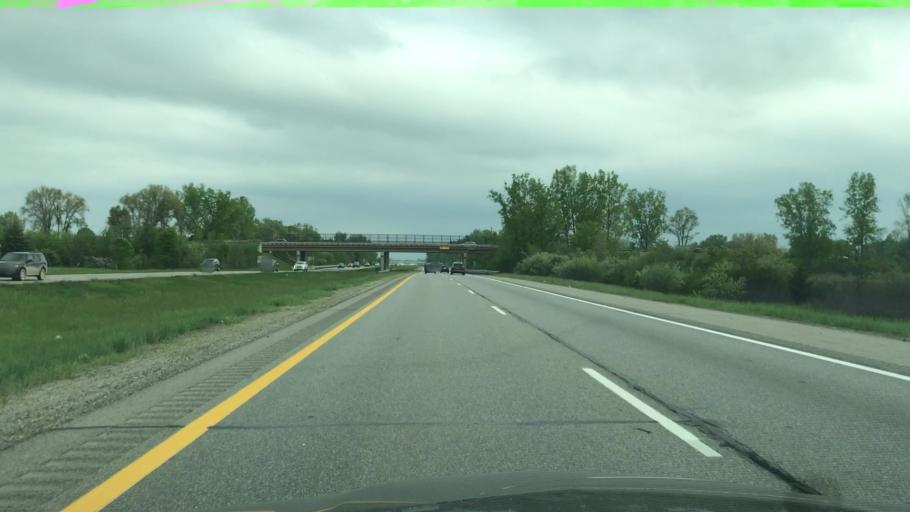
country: US
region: Michigan
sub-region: Macomb County
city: Utica
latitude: 42.6428
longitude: -83.0140
